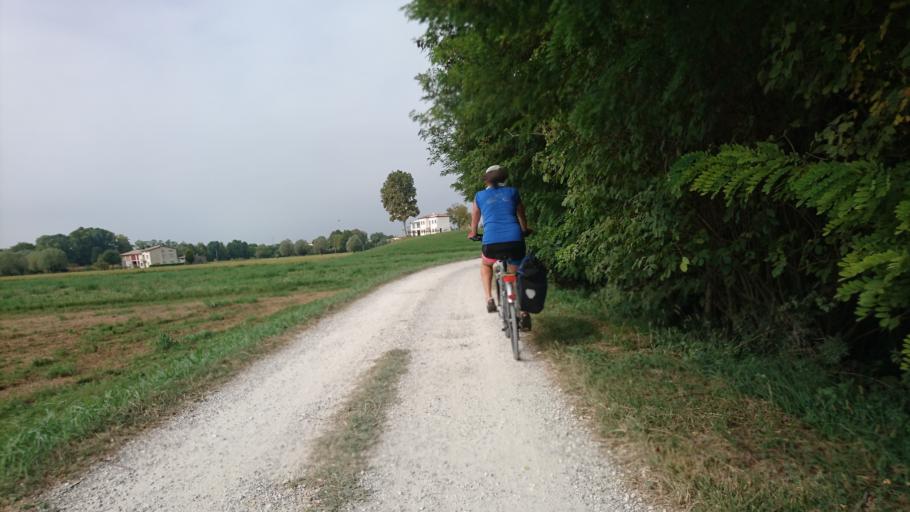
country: IT
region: Veneto
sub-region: Provincia di Padova
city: Grantorto
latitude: 45.5820
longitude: 11.7524
